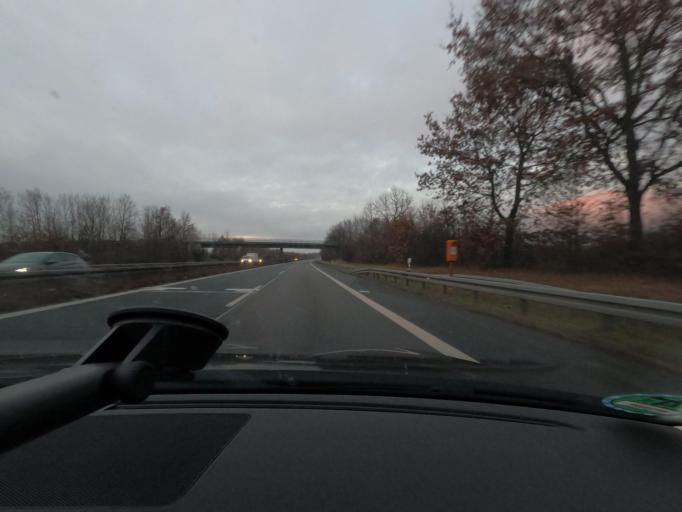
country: DE
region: Bavaria
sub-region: Upper Franconia
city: Altendorf
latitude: 49.8086
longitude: 11.0139
